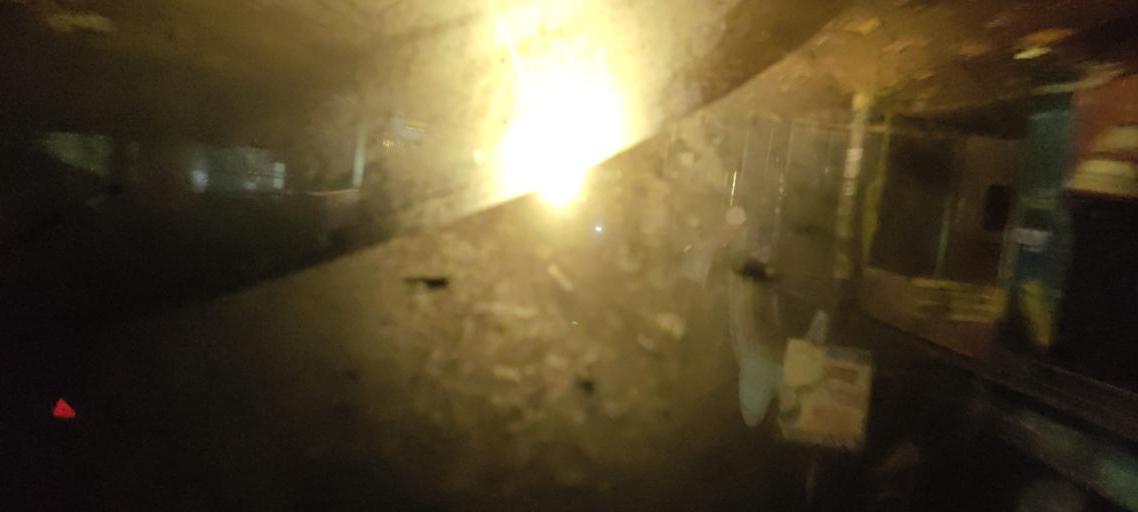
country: IN
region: Kerala
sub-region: Alappuzha
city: Vayalar
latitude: 9.7225
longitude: 76.3376
